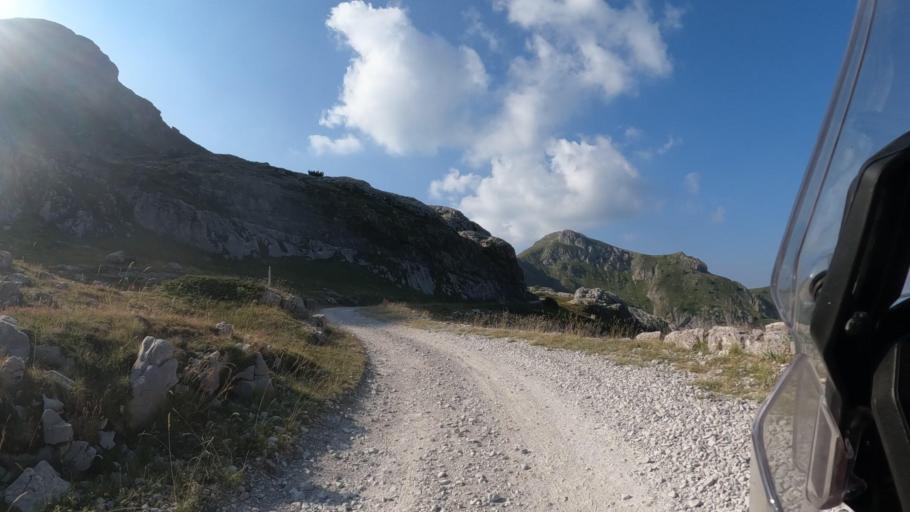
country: IT
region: Piedmont
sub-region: Provincia di Cuneo
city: Limone Piemonte
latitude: 44.1631
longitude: 7.6695
